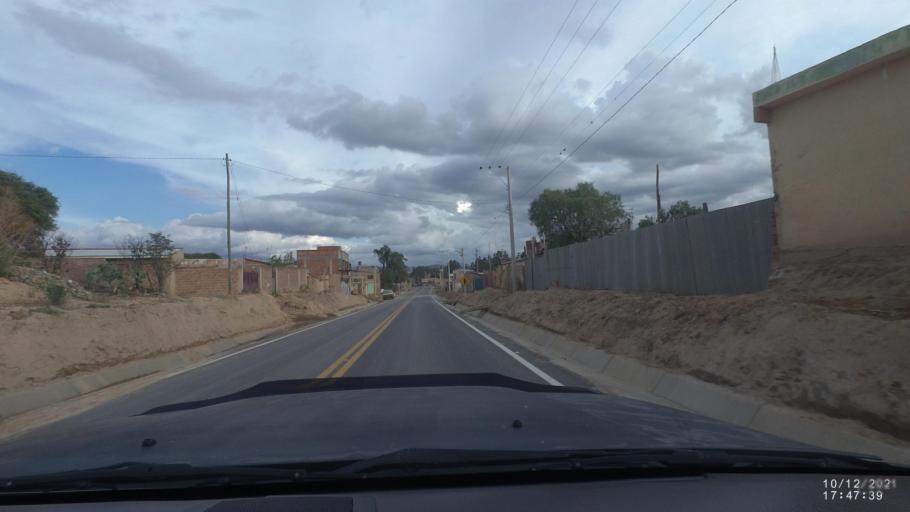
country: BO
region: Cochabamba
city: Tarata
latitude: -17.6396
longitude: -65.9831
